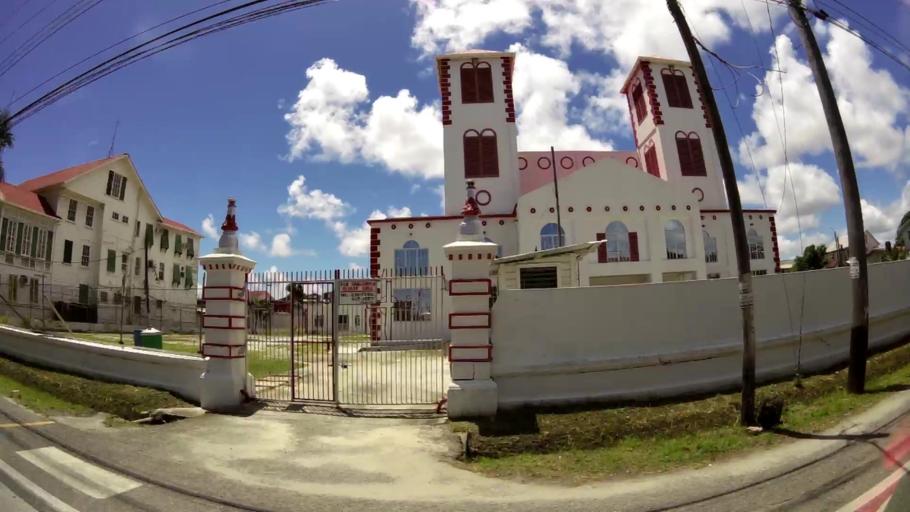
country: GY
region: Demerara-Mahaica
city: Georgetown
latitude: 6.8160
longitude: -58.1644
